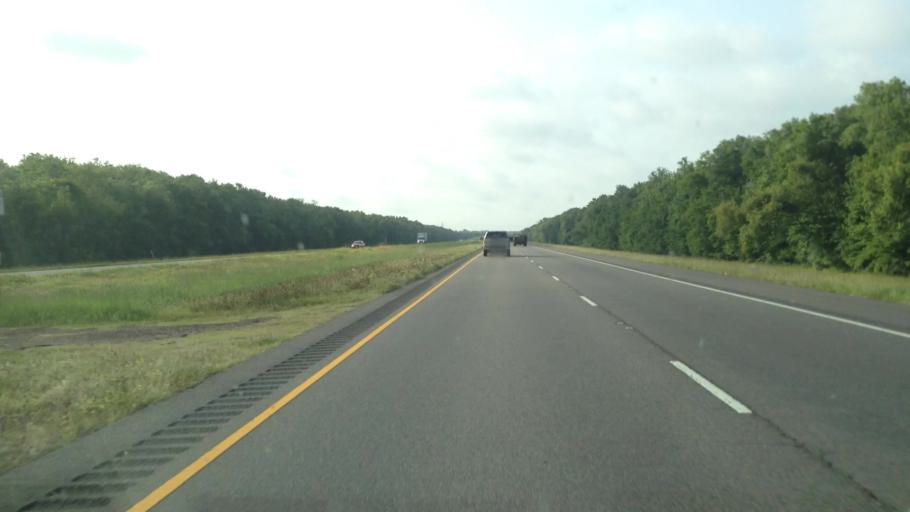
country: US
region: Louisiana
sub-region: Avoyelles Parish
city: Bunkie
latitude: 30.9105
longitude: -92.2396
